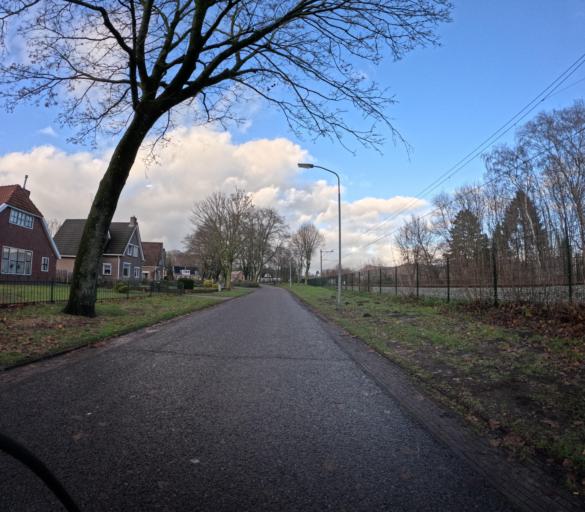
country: NL
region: Drenthe
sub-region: Gemeente Emmen
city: Emmen
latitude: 52.7740
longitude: 6.8995
